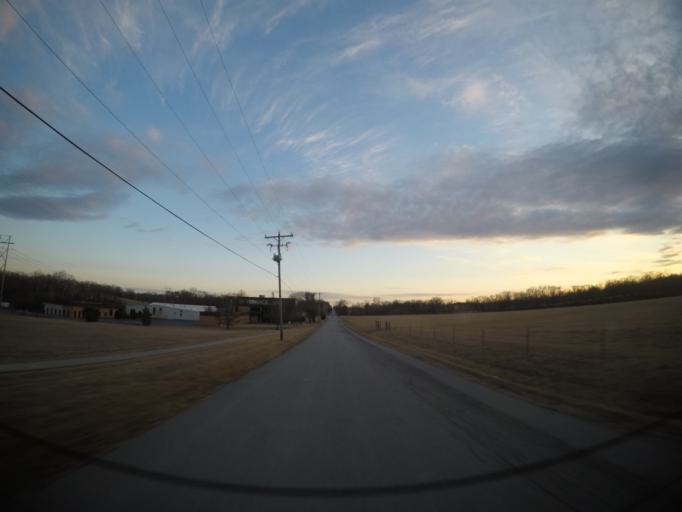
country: US
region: Kansas
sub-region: Wyandotte County
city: Bonner Springs
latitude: 39.0539
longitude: -94.9088
